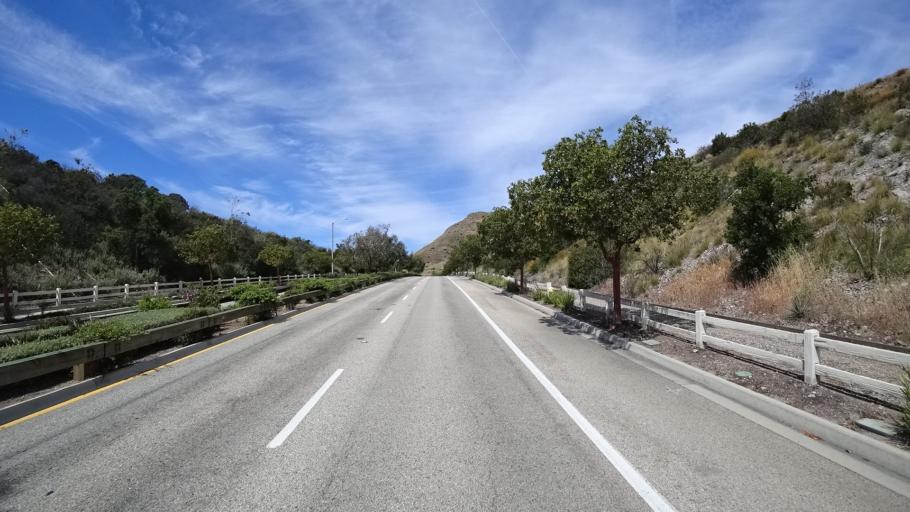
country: US
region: California
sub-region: Ventura County
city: Casa Conejo
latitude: 34.1802
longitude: -118.9684
